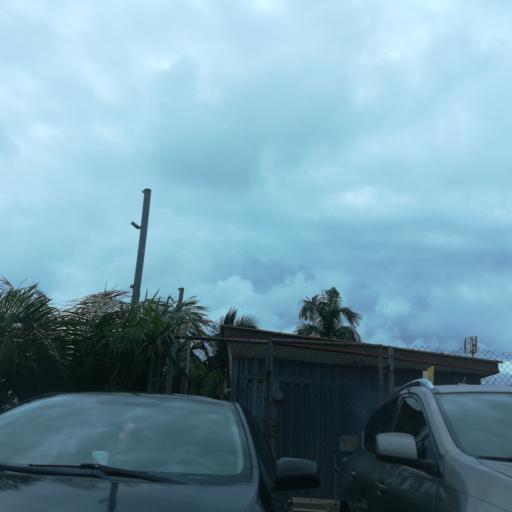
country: NG
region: Lagos
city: Ikoyi
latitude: 6.4459
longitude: 3.4541
